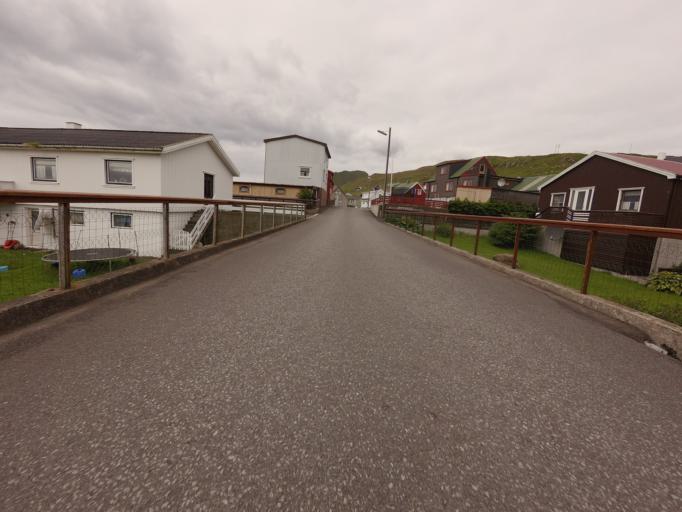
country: FO
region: Suduroy
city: Vagur
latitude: 61.4028
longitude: -6.7111
